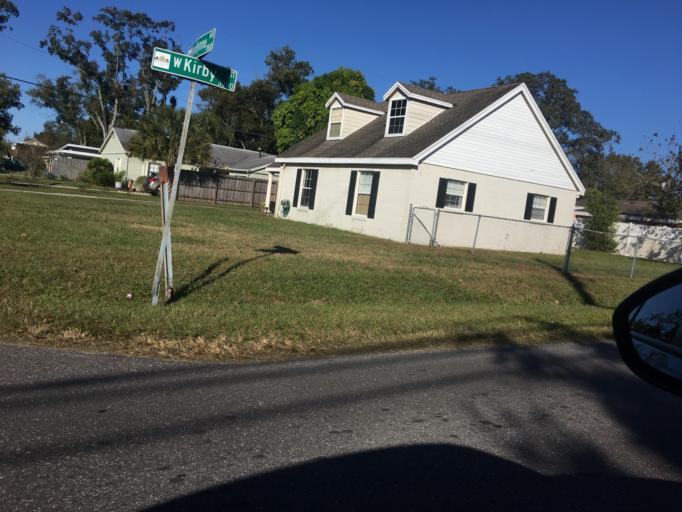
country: US
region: Florida
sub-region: Hillsborough County
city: Egypt Lake-Leto
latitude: 28.0181
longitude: -82.4930
